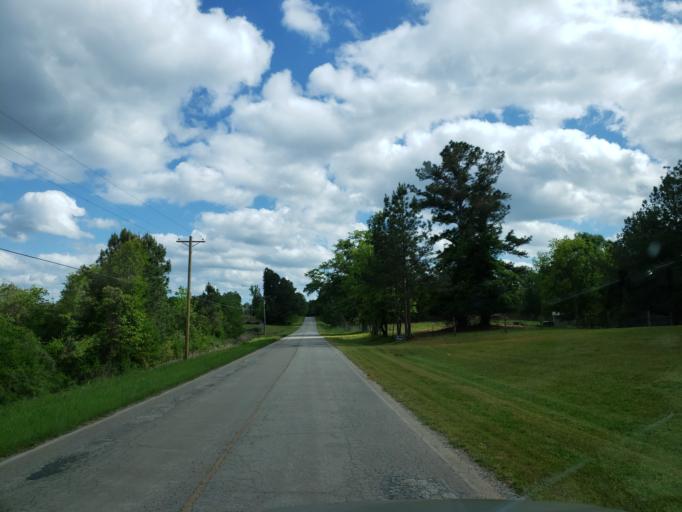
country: US
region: Georgia
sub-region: Haralson County
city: Tallapoosa
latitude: 33.6980
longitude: -85.3264
